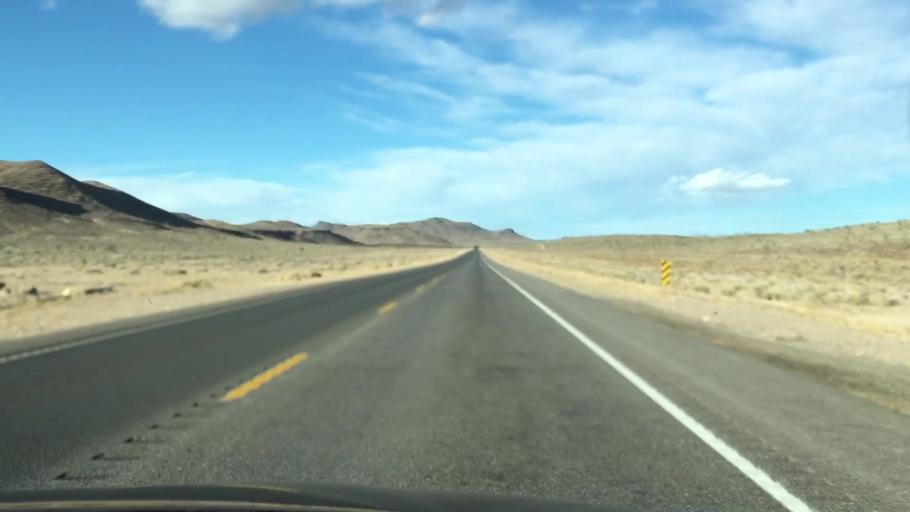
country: US
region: Nevada
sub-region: Esmeralda County
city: Goldfield
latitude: 37.6271
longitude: -117.2186
